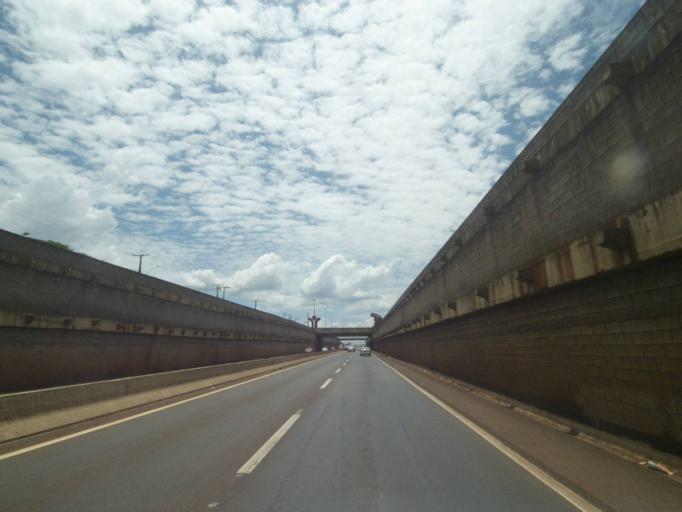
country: BR
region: Parana
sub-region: Londrina
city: Londrina
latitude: -23.3126
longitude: -51.2150
